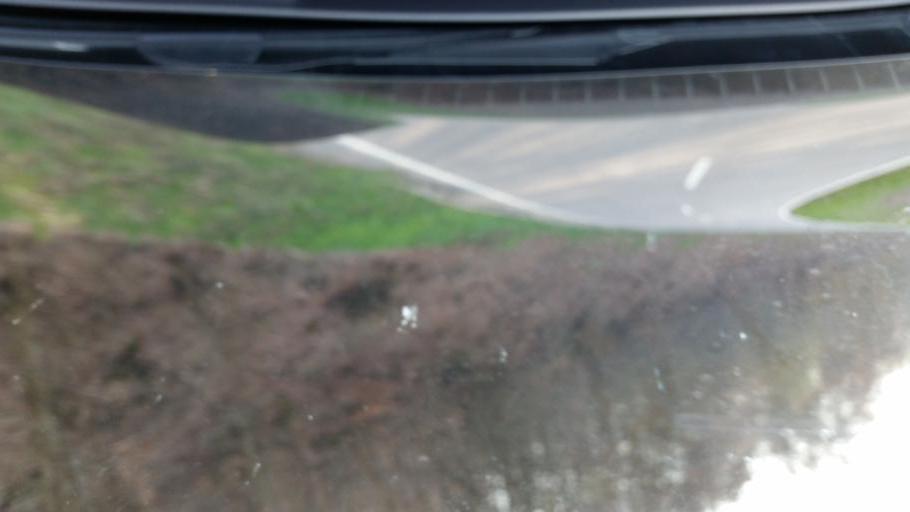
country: DE
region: Baden-Wuerttemberg
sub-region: Karlsruhe Region
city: Billigheim
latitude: 49.3608
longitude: 9.2598
